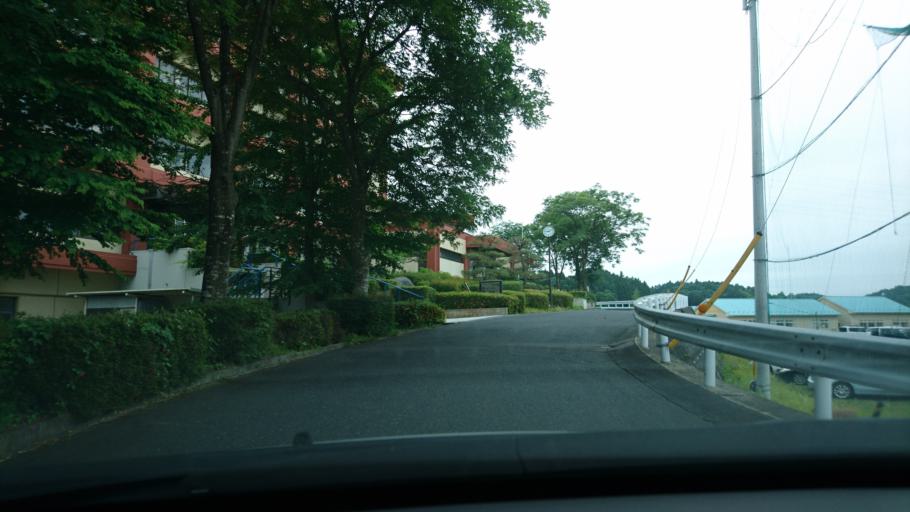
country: JP
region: Iwate
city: Ichinoseki
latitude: 38.9143
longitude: 141.1106
